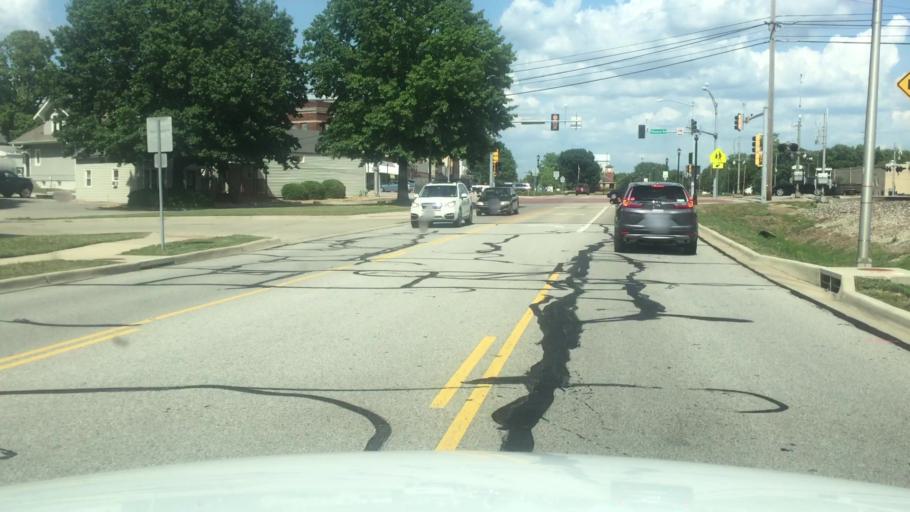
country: US
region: Kansas
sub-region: Johnson County
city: Lenexa
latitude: 38.9599
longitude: -94.7430
